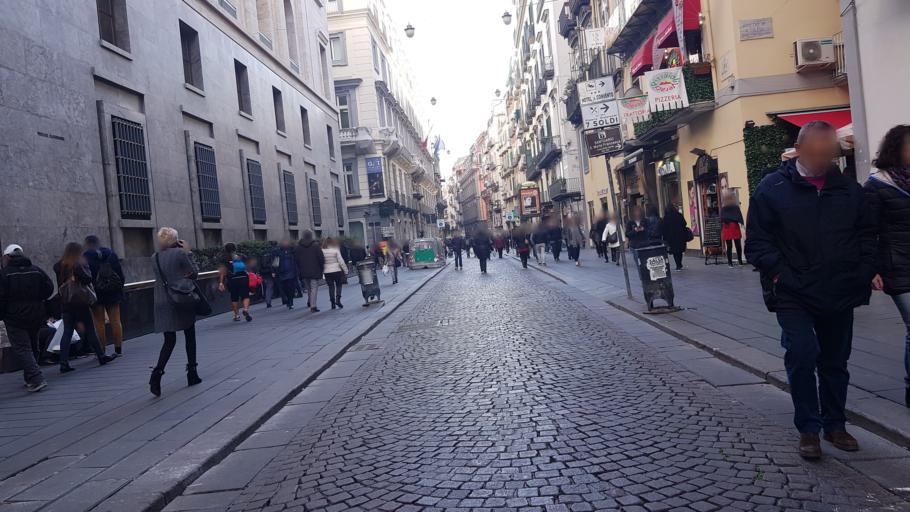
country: IT
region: Campania
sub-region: Provincia di Napoli
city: Napoli
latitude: 40.8405
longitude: 14.2486
